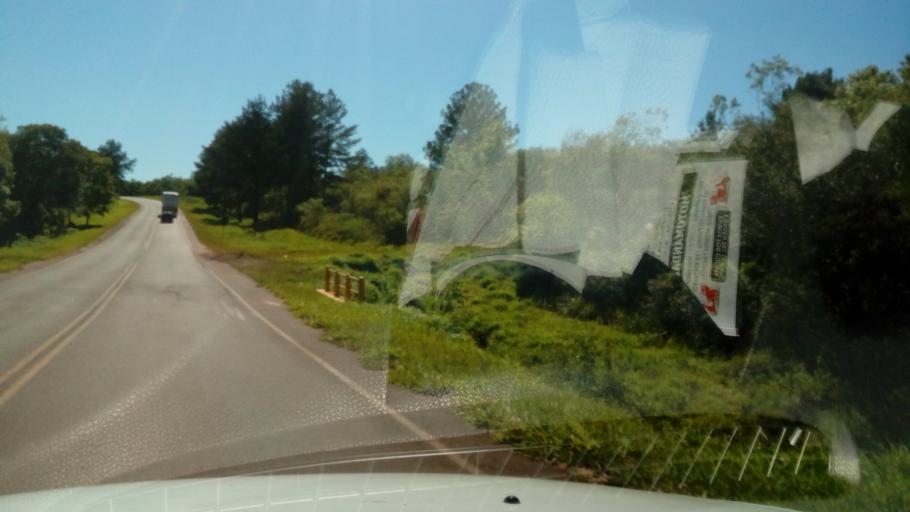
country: AR
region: Misiones
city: Santa Ana
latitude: -27.4177
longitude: -55.5333
